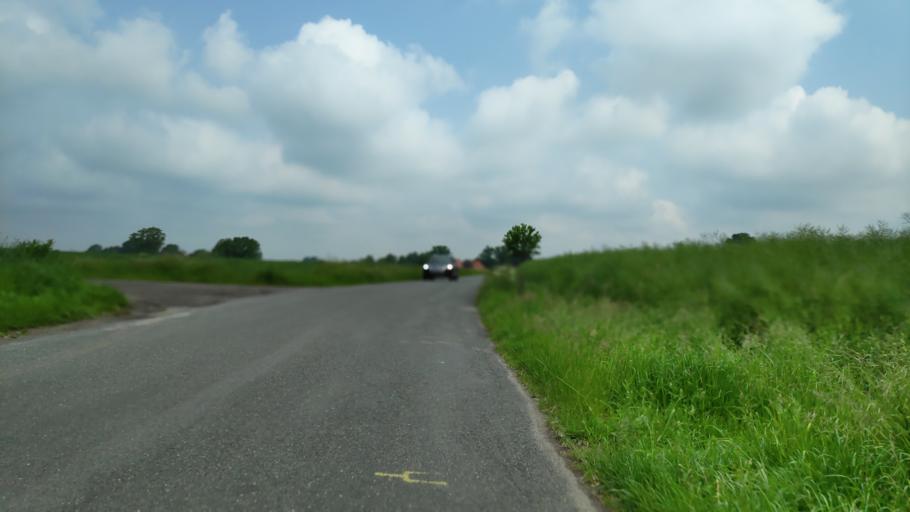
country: DE
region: North Rhine-Westphalia
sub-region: Regierungsbezirk Detmold
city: Hille
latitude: 52.3480
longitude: 8.7614
